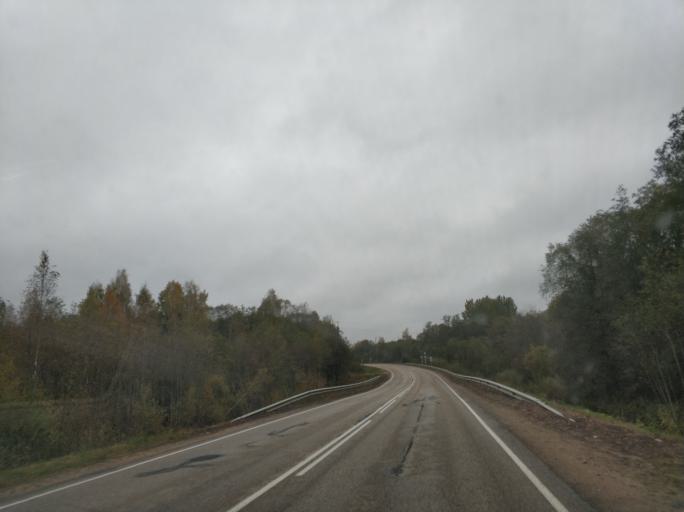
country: BY
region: Vitebsk
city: Rasony
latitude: 56.0597
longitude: 28.7147
